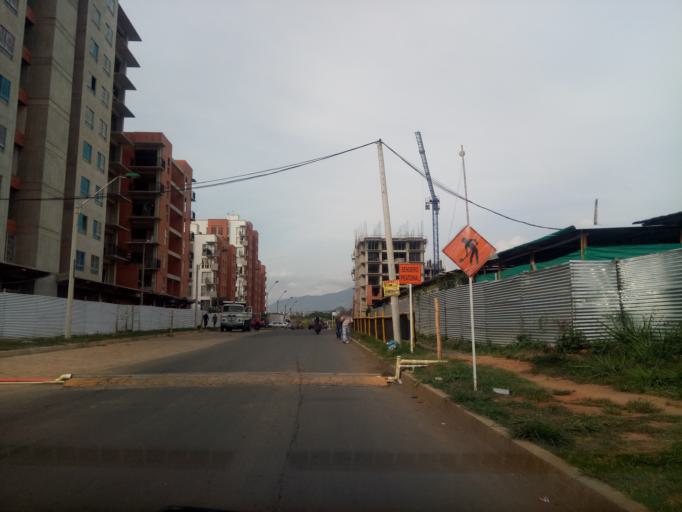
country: CO
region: Valle del Cauca
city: Cali
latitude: 3.3674
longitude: -76.5076
